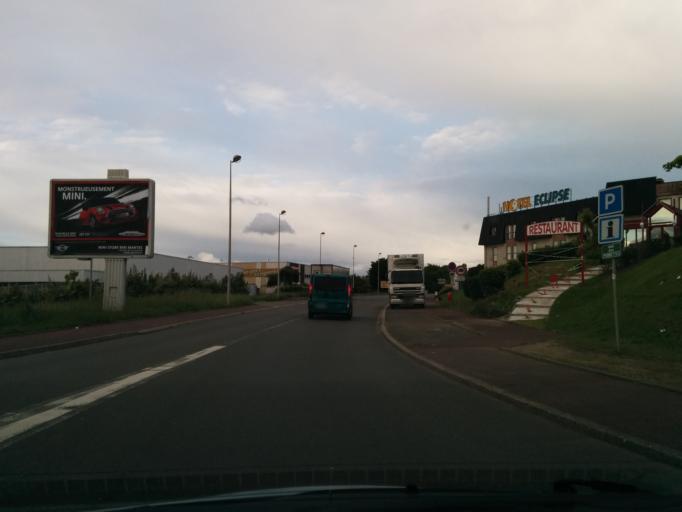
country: FR
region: Ile-de-France
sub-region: Departement des Yvelines
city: Mantes-la-Ville
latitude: 48.9772
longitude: 1.6936
